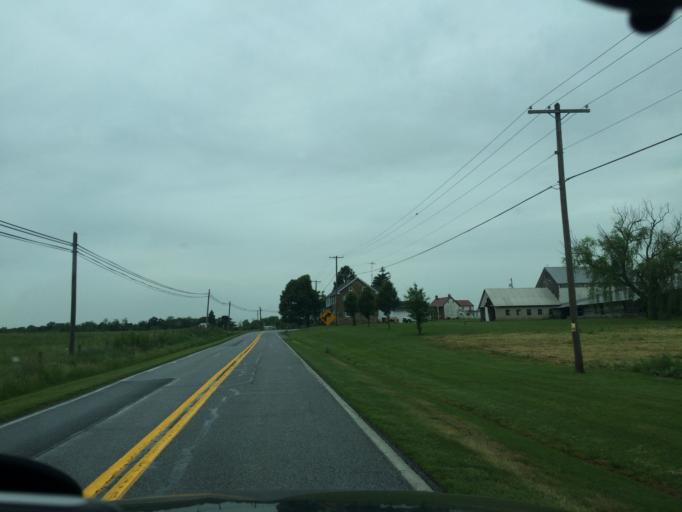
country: US
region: Maryland
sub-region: Carroll County
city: Taneytown
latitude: 39.5960
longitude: -77.2252
